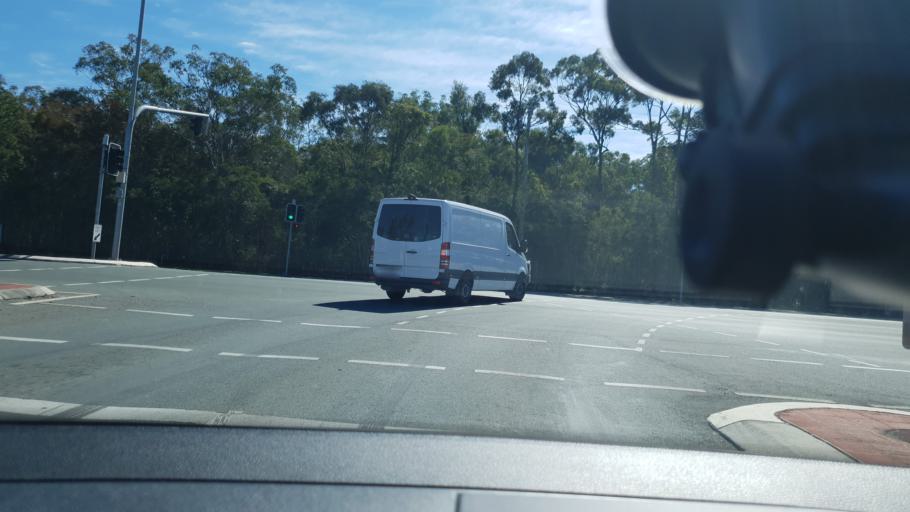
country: AU
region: Queensland
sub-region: Logan
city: Woodridge
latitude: -27.6453
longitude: 153.0943
